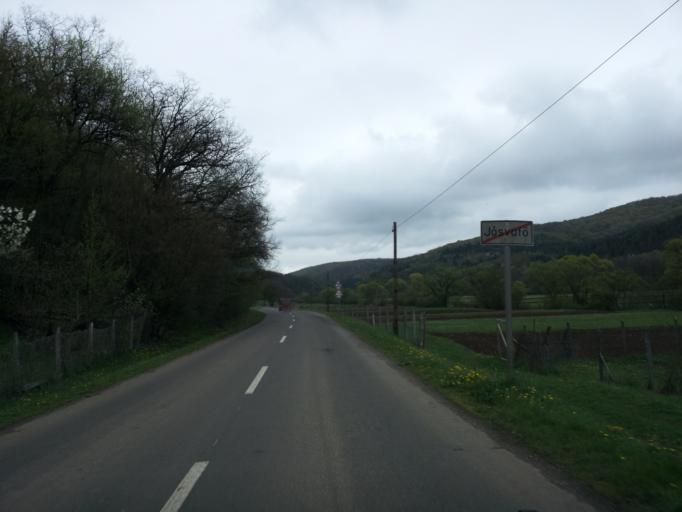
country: HU
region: Borsod-Abauj-Zemplen
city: Rudabanya
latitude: 48.4824
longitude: 20.5597
